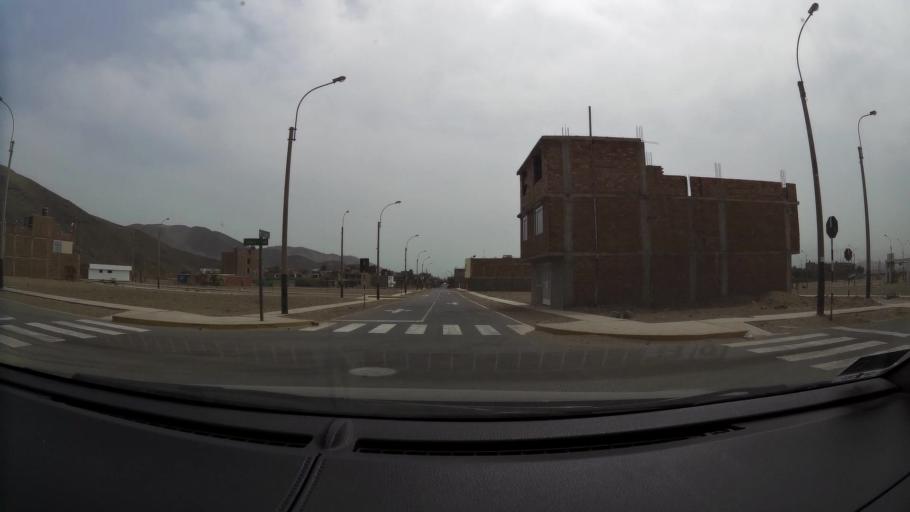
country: PE
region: Lima
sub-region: Lima
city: Santa Rosa
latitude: -11.7919
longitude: -77.1510
